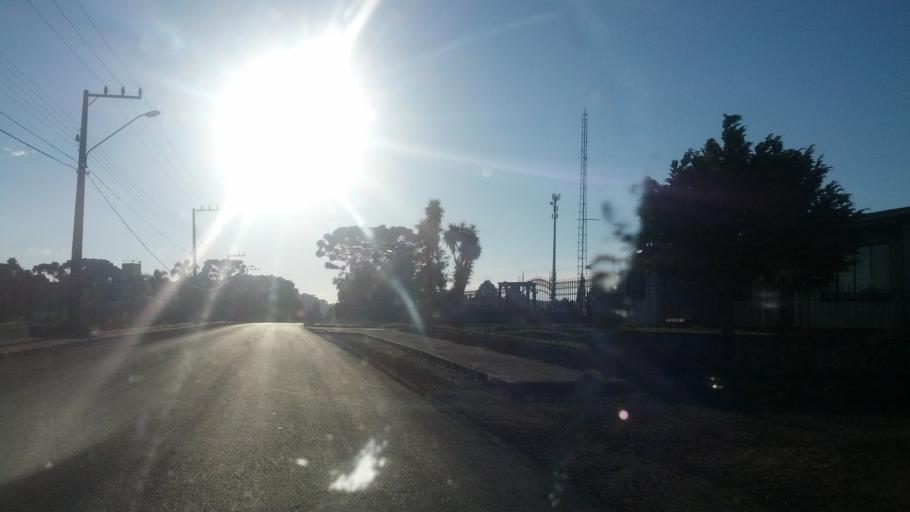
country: BR
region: Rio Grande do Sul
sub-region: Vacaria
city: Estrela
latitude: -27.8966
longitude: -50.7644
